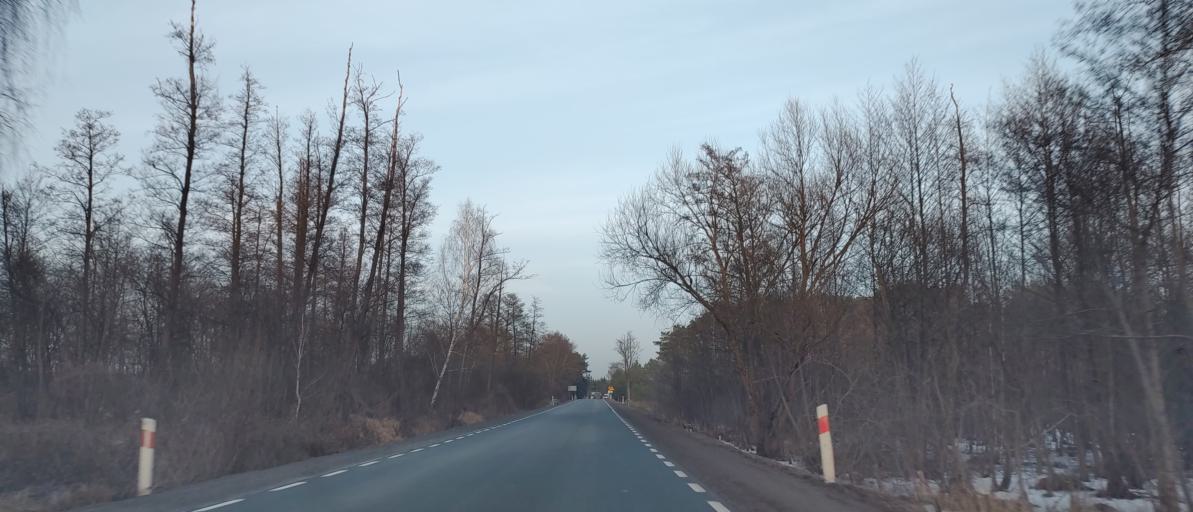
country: PL
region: Masovian Voivodeship
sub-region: Powiat bialobrzeski
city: Bialobrzegi
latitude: 51.6423
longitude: 20.9194
